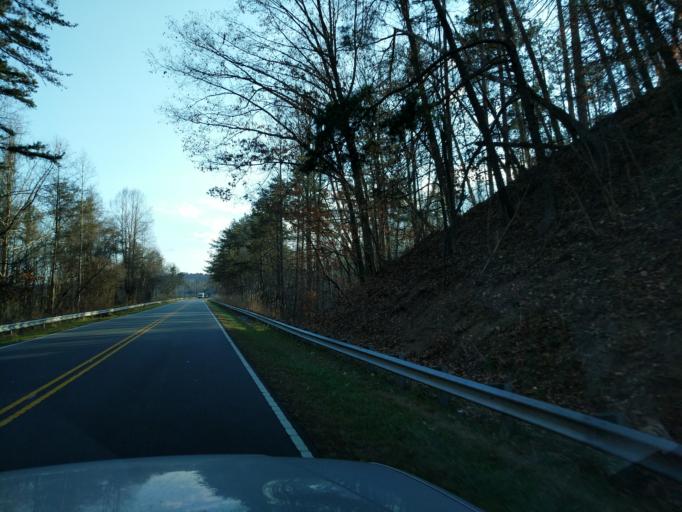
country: US
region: North Carolina
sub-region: McDowell County
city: West Marion
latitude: 35.5184
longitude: -81.9736
